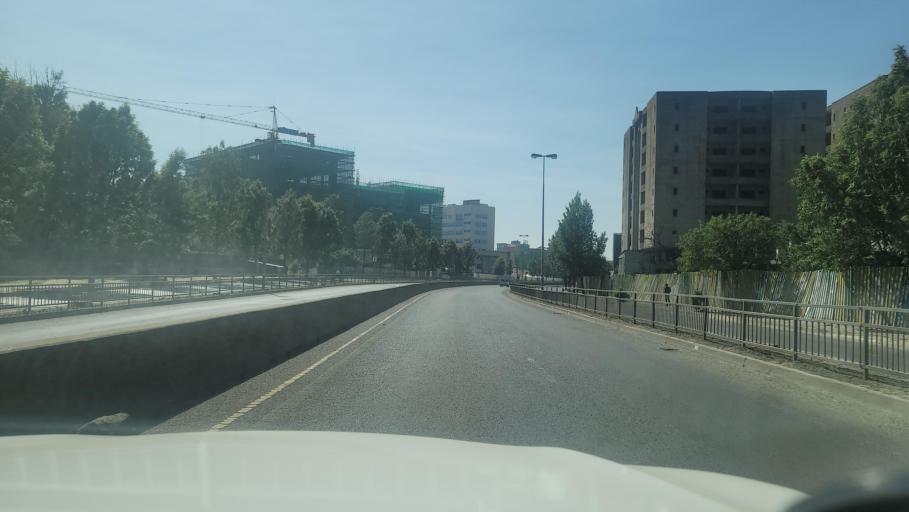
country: ET
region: Adis Abeba
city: Addis Ababa
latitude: 9.0133
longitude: 38.8038
